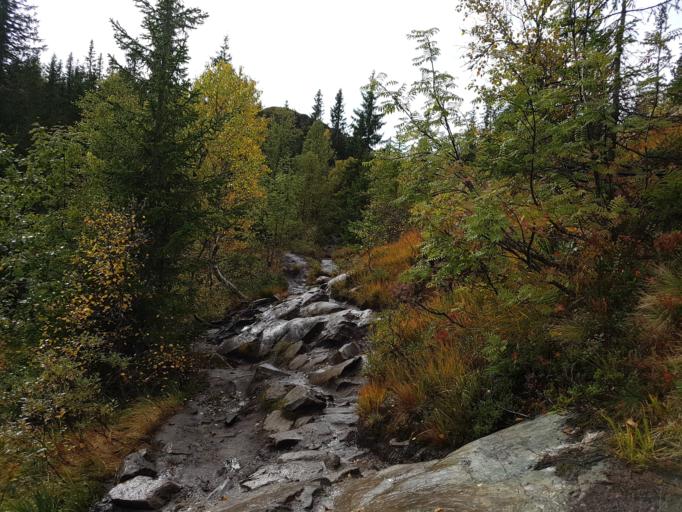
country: NO
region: Sor-Trondelag
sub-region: Melhus
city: Melhus
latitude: 63.4069
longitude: 10.2054
